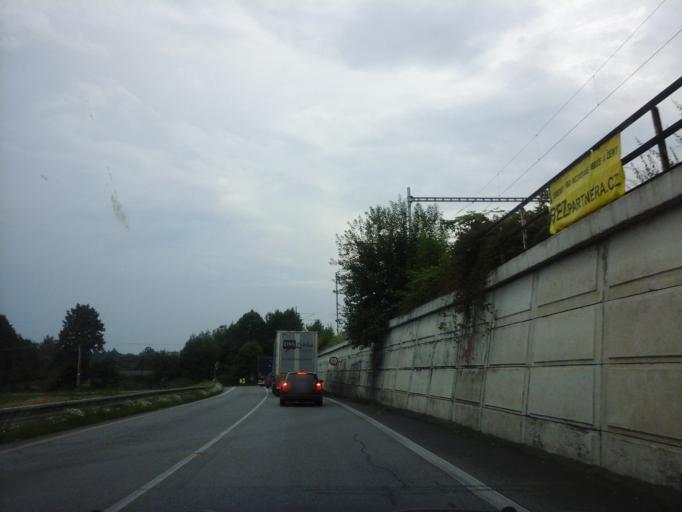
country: CZ
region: South Moravian
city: Svitavka
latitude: 49.5092
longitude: 16.5856
